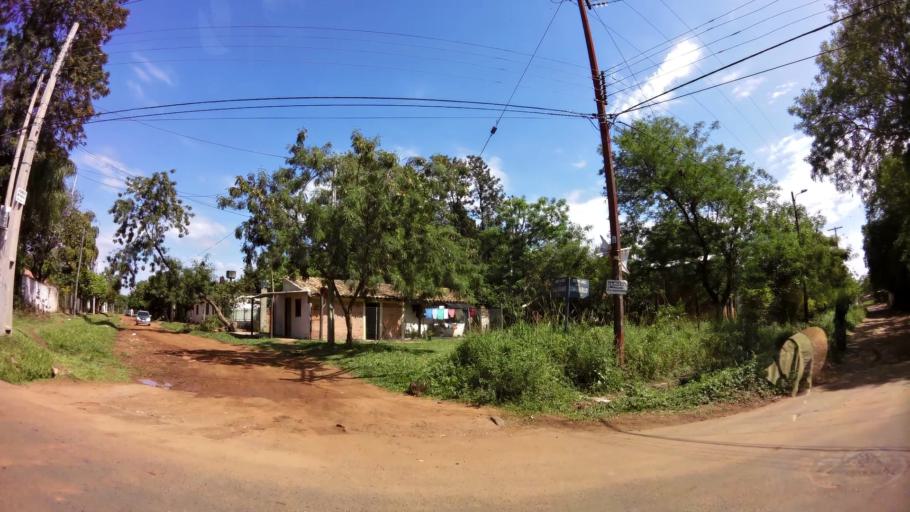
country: PY
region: Central
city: Limpio
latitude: -25.2509
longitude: -57.4913
